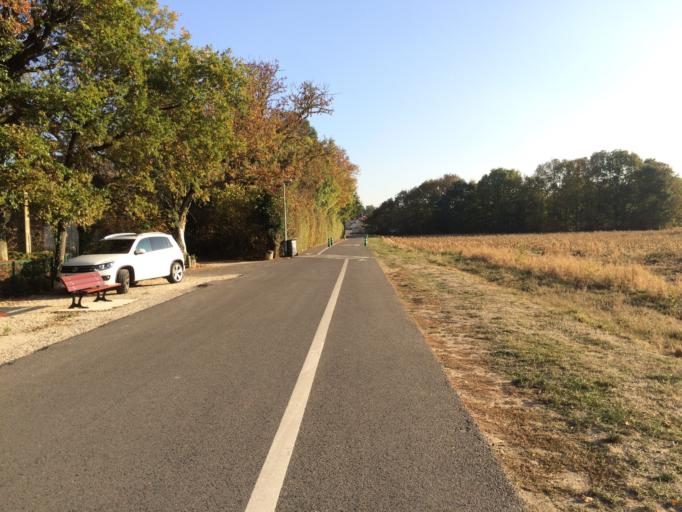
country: FR
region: Ile-de-France
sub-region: Departement de l'Essonne
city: Villejust
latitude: 48.6822
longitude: 2.2419
